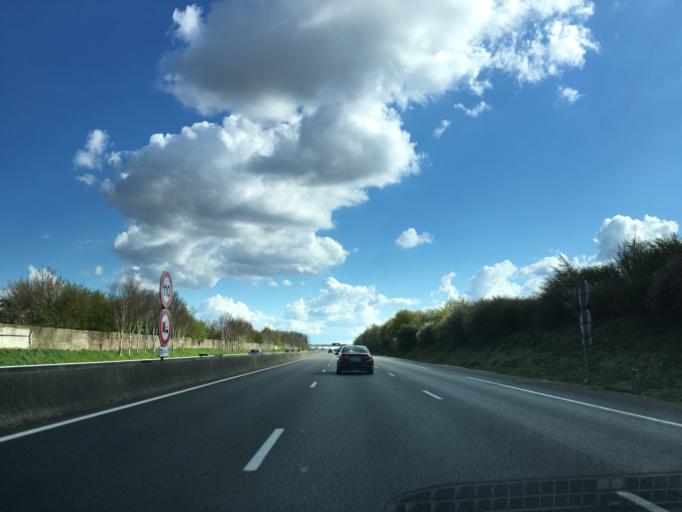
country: FR
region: Nord-Pas-de-Calais
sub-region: Departement du Pas-de-Calais
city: Bapaume
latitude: 50.1317
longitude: 2.8715
